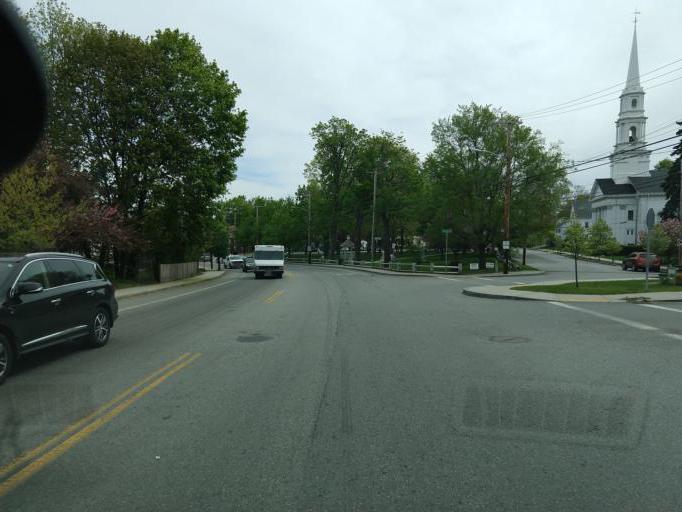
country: US
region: Massachusetts
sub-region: Essex County
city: Haverhill
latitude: 42.7669
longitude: -71.0774
